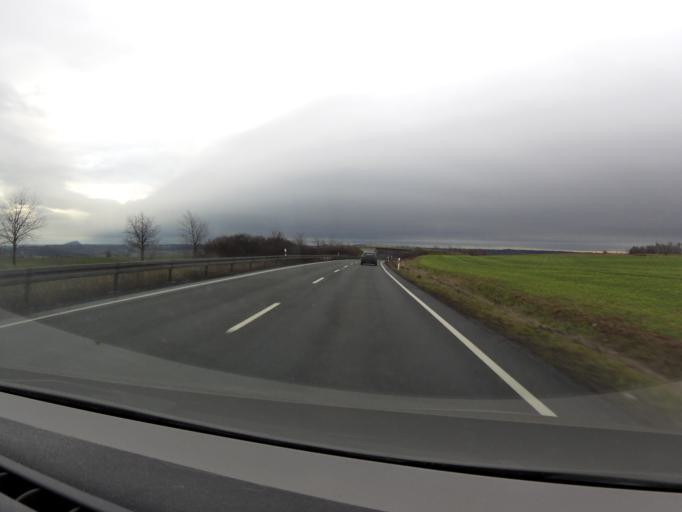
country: DE
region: Saxony-Anhalt
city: Grossorner
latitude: 51.6361
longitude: 11.4771
